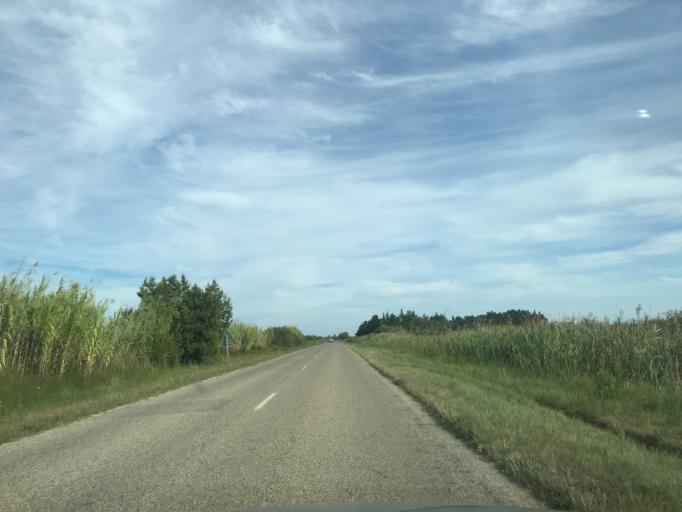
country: FR
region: Provence-Alpes-Cote d'Azur
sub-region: Departement des Bouches-du-Rhone
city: Saintes-Maries-de-la-Mer
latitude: 43.5245
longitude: 4.3798
